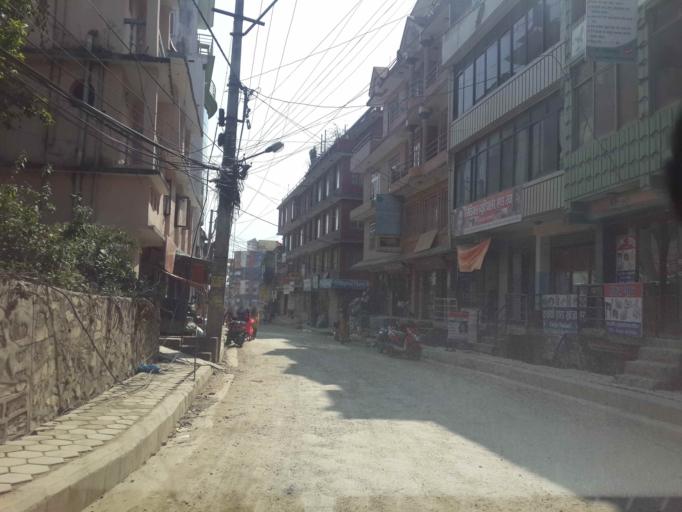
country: NP
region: Central Region
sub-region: Bagmati Zone
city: Kathmandu
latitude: 27.7327
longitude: 85.3451
